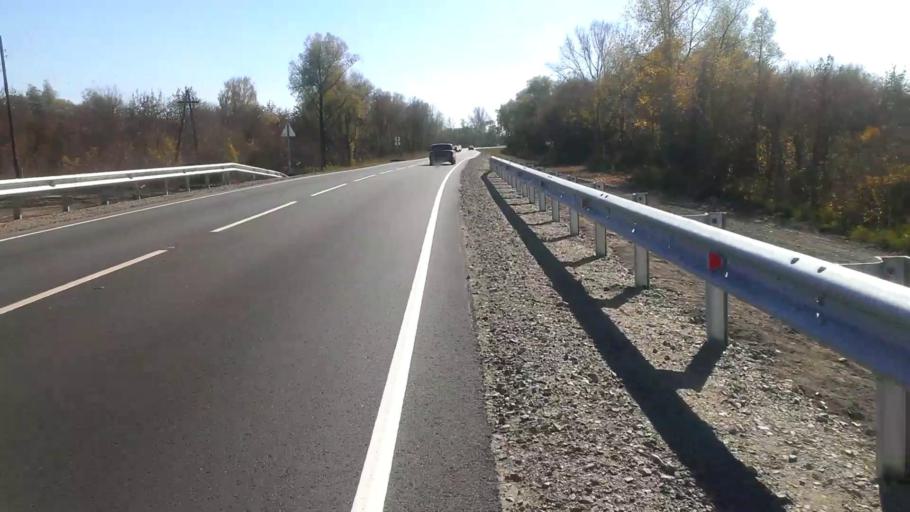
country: RU
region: Altai Krai
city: Sannikovo
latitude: 53.3267
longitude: 83.9417
